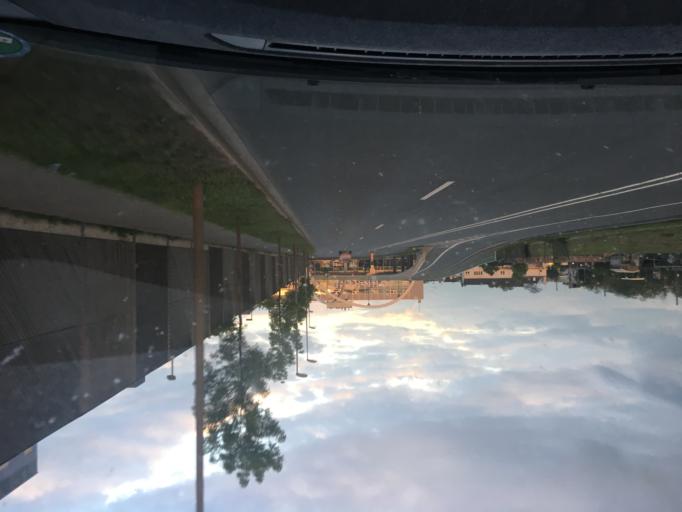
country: DE
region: North Rhine-Westphalia
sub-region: Regierungsbezirk Dusseldorf
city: Dusseldorf
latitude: 51.2100
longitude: 6.7552
